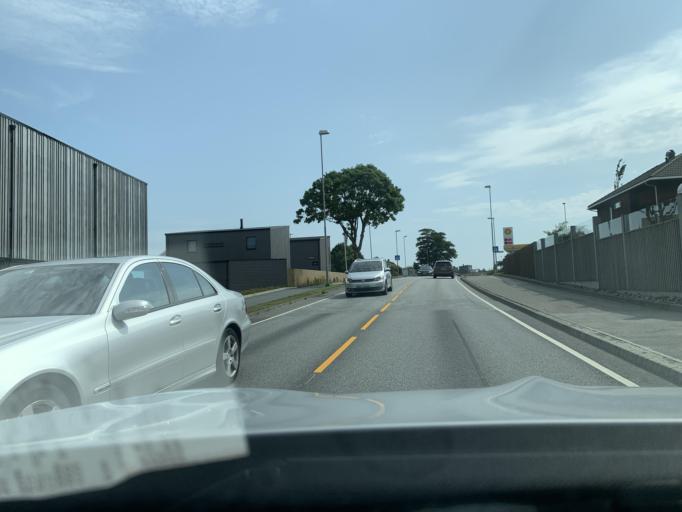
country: NO
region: Rogaland
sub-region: Klepp
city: Kleppe
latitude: 58.7716
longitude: 5.6300
